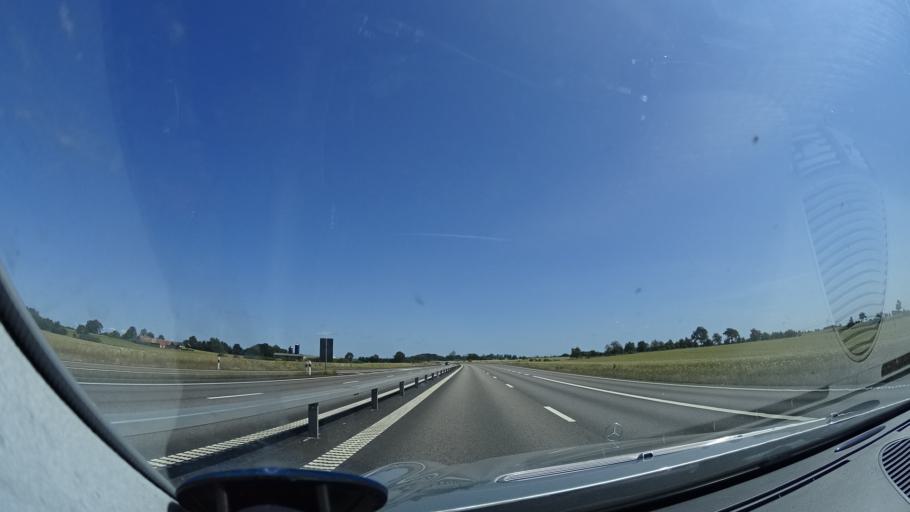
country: SE
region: Skane
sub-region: Hoors Kommun
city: Loberod
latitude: 55.8244
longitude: 13.5284
